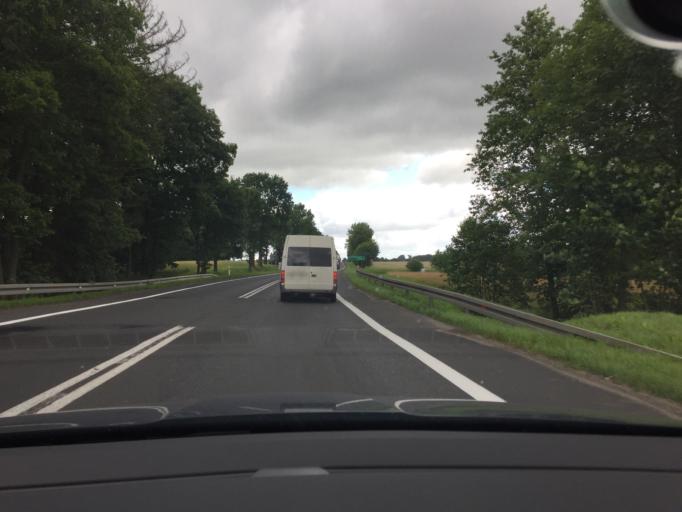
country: PL
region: West Pomeranian Voivodeship
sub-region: Powiat bialogardzki
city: Bialogard
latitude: 54.1076
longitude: 15.9978
